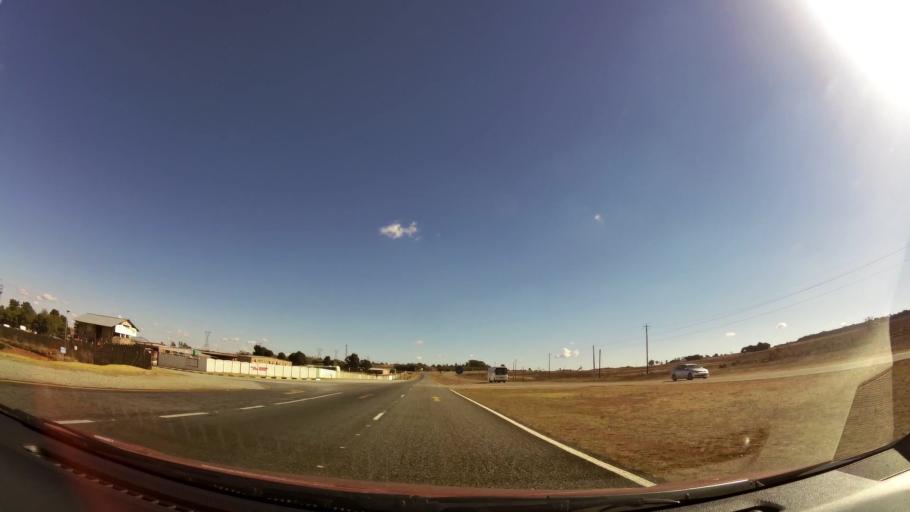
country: ZA
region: Gauteng
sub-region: West Rand District Municipality
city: Carletonville
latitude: -26.4164
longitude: 27.4477
